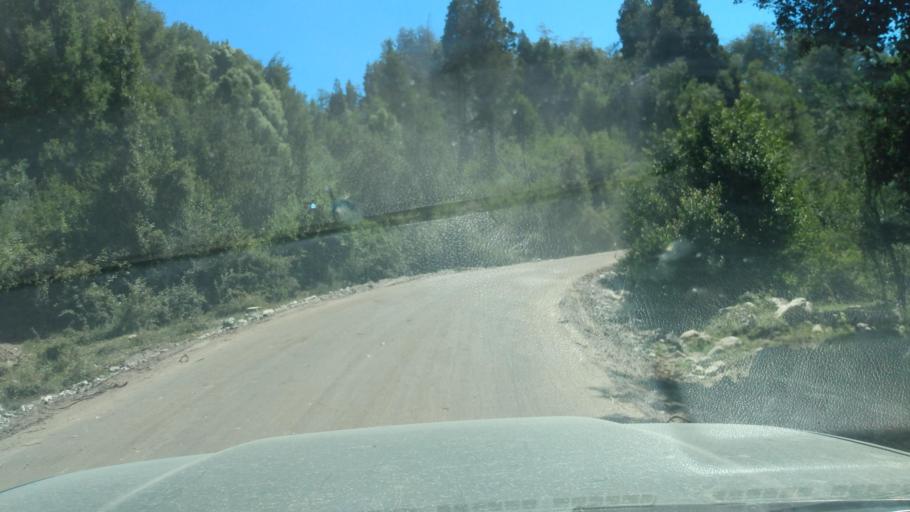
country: AR
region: Neuquen
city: Villa La Angostura
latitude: -40.6169
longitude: -71.5319
